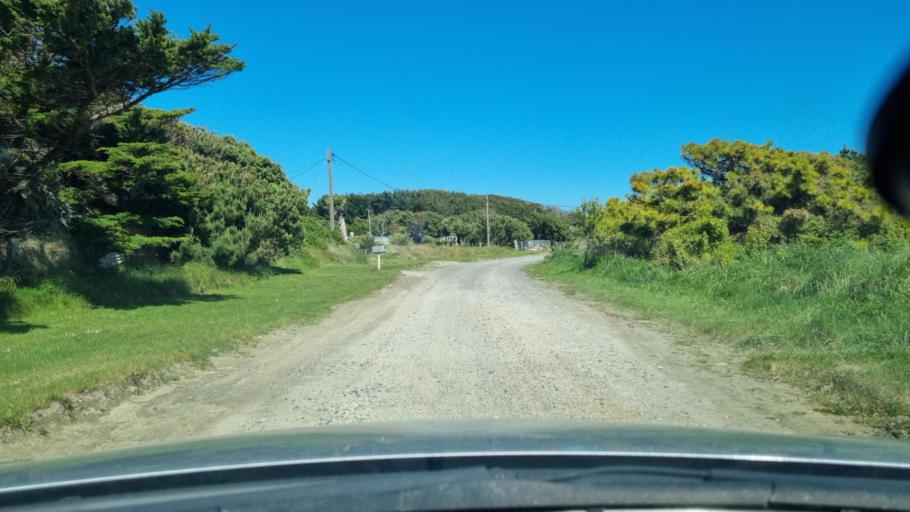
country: NZ
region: Southland
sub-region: Invercargill City
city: Invercargill
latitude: -46.4380
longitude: 168.2372
